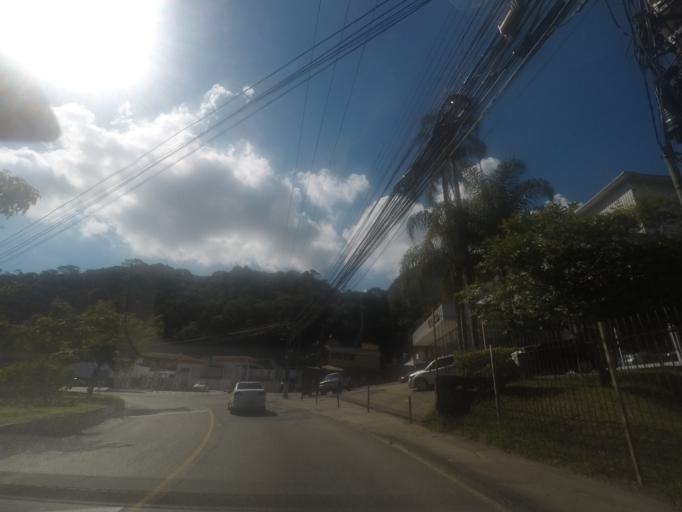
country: BR
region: Rio de Janeiro
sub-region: Petropolis
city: Petropolis
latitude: -22.5329
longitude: -43.2044
